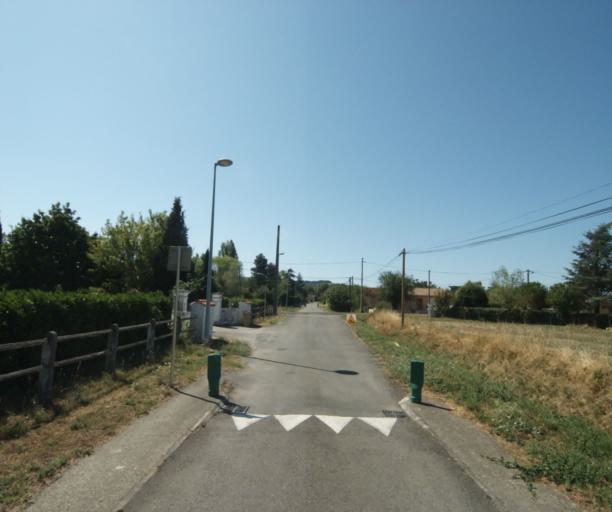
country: FR
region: Midi-Pyrenees
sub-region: Departement de la Haute-Garonne
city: Revel
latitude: 43.4664
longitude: 1.9985
